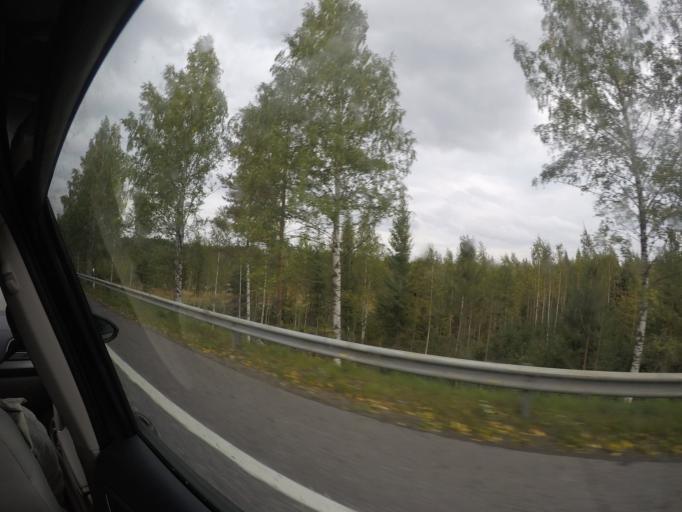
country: FI
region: Haeme
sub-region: Haemeenlinna
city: Parola
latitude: 61.1716
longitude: 24.4114
